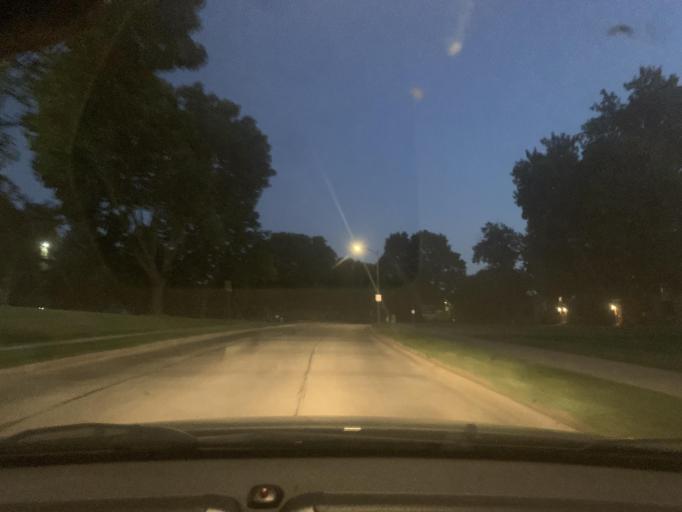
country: US
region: Nebraska
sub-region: Sarpy County
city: La Vista
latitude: 41.1793
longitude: -96.0475
